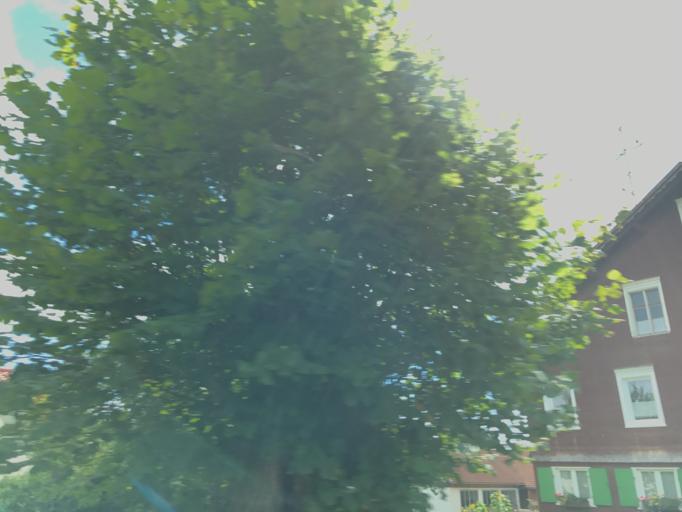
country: DE
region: Bavaria
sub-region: Swabia
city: Rothenbach
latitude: 47.6399
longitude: 9.9554
